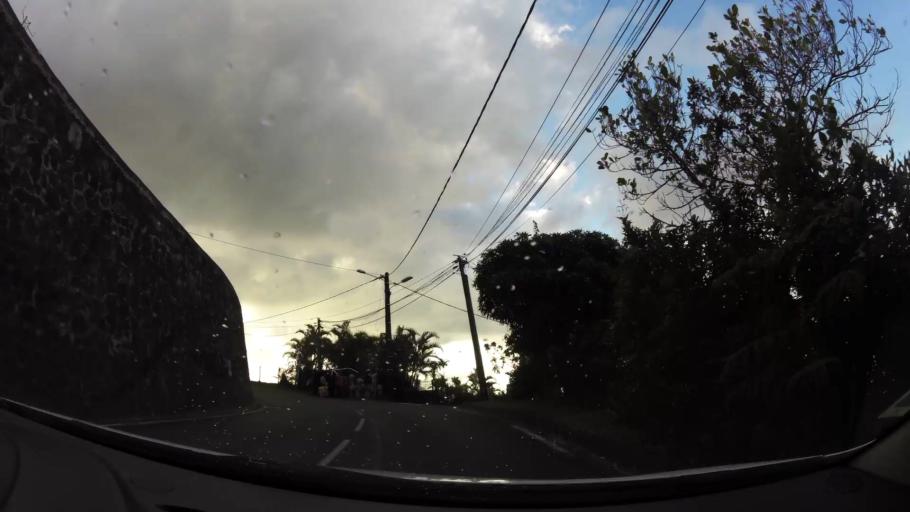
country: RE
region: Reunion
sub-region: Reunion
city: Saint-Denis
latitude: -20.9150
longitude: 55.4393
